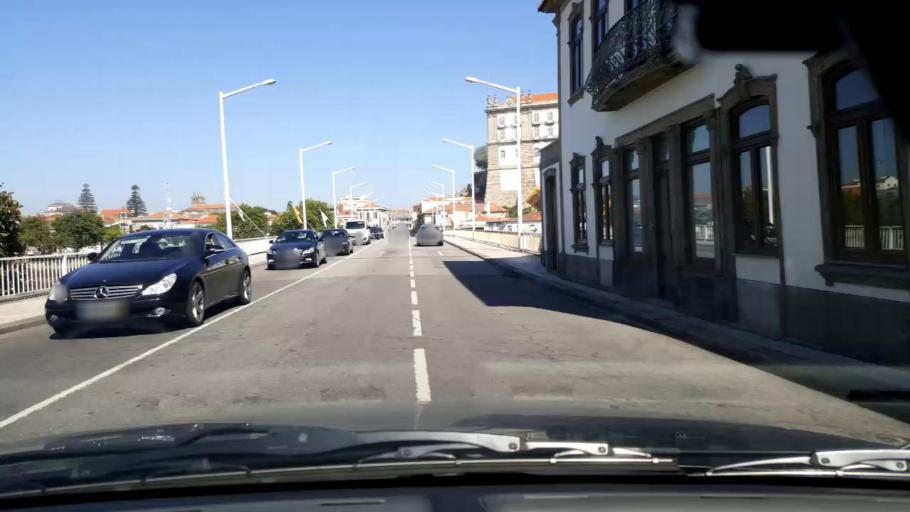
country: PT
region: Porto
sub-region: Vila do Conde
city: Vila do Conde
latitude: 41.3504
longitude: -8.7390
